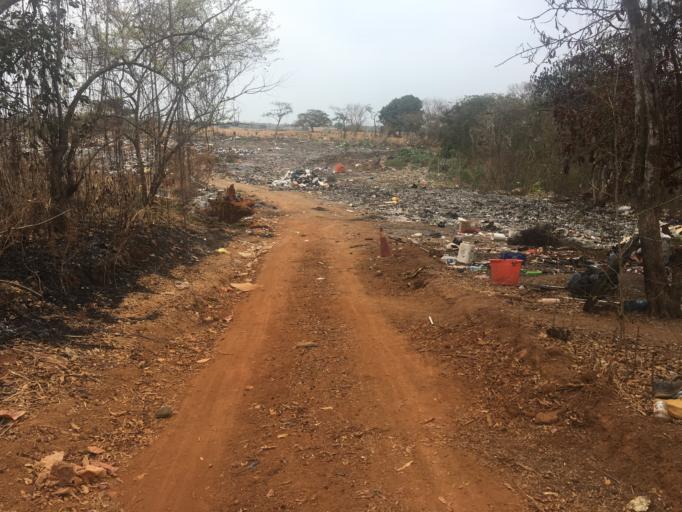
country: PA
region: Los Santos
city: Pedasi
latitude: 7.5487
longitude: -80.0834
